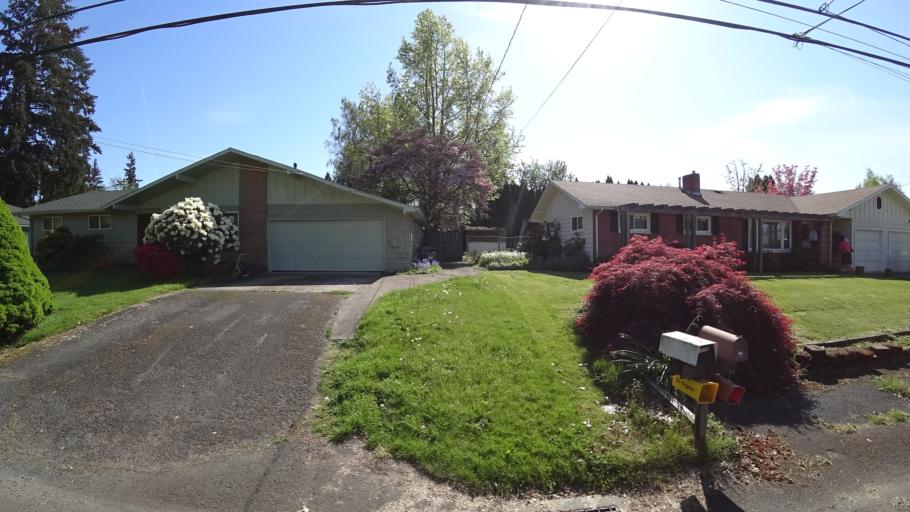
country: US
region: Oregon
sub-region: Washington County
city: Hillsboro
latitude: 45.5262
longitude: -122.9719
